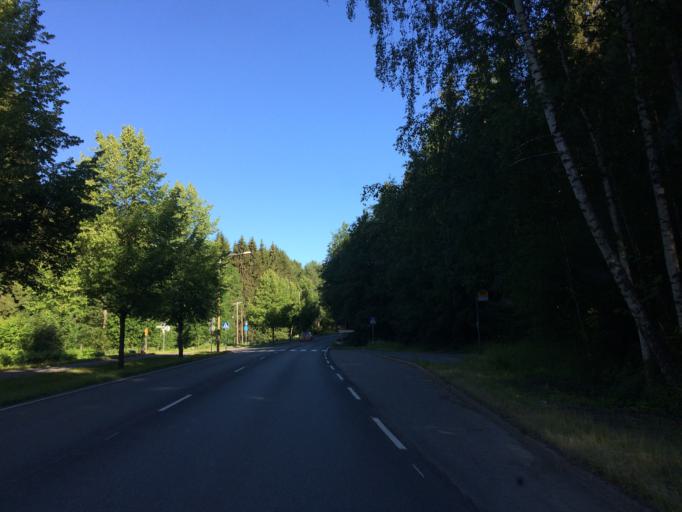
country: FI
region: Haeme
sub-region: Haemeenlinna
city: Haemeenlinna
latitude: 60.9681
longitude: 24.4408
